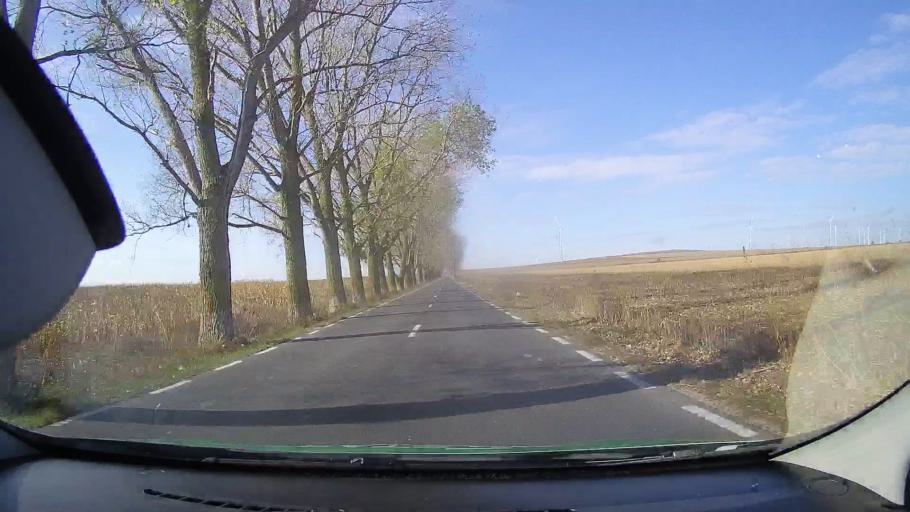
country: RO
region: Tulcea
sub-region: Comuna Valea Nucarilor
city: Iazurile
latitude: 45.0263
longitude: 29.0000
